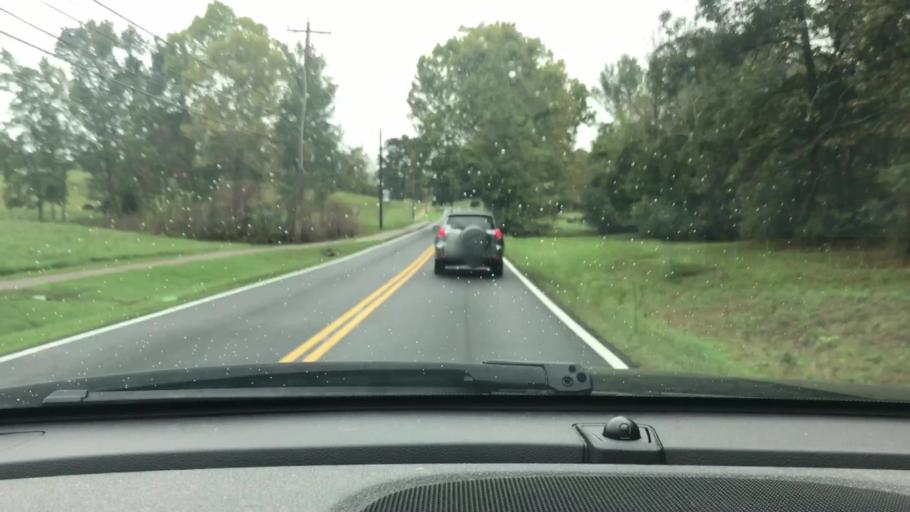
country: US
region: Tennessee
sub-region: Cheatham County
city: Kingston Springs
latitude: 36.0955
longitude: -87.1113
